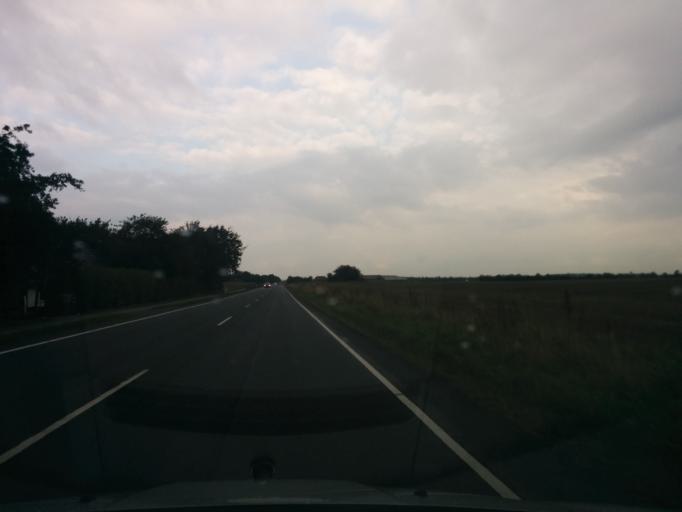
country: DK
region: South Denmark
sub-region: Esbjerg Kommune
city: Bramming
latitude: 55.5811
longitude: 8.6917
